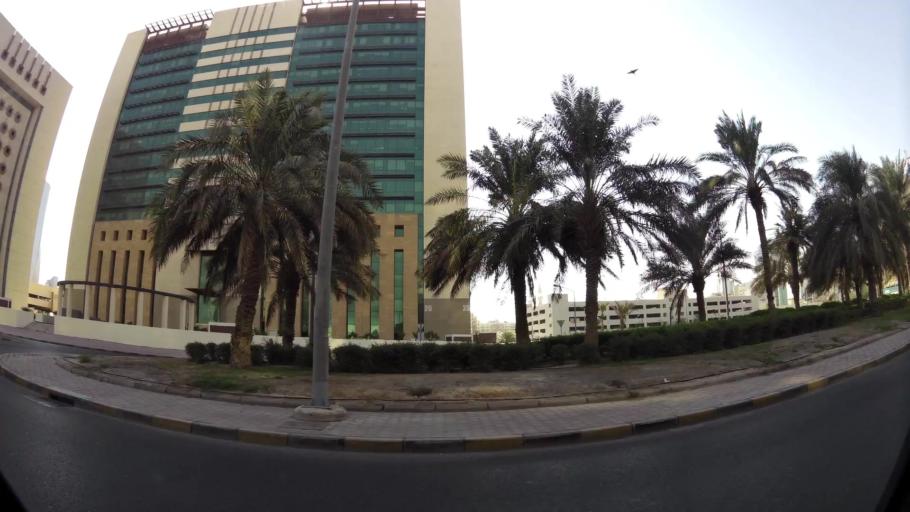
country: KW
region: Al Asimah
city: Kuwait City
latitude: 29.3791
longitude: 47.9804
